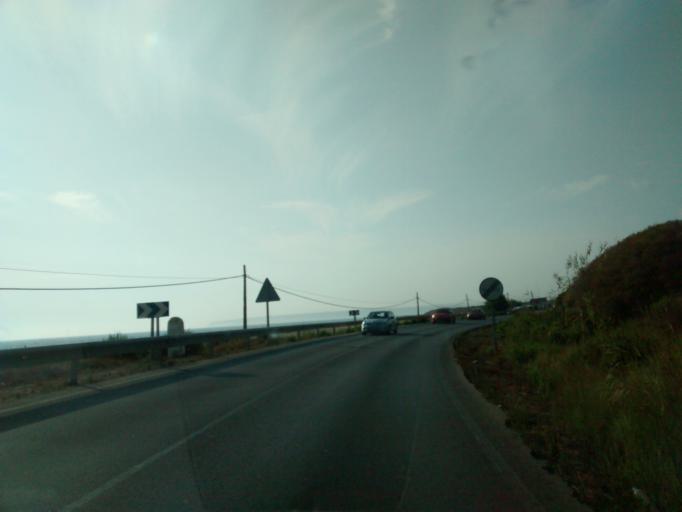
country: ES
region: Andalusia
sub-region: Provincia de Cadiz
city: Zahara de los Atunes
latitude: 36.1392
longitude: -5.8508
